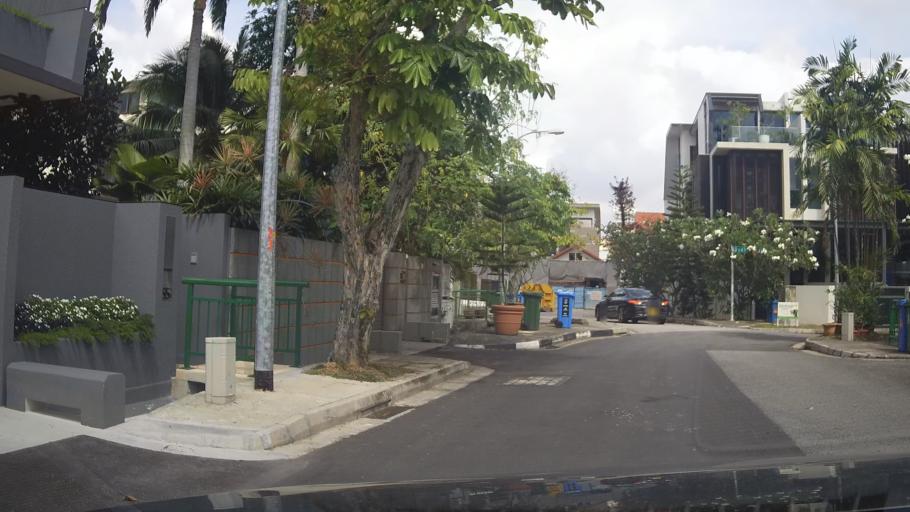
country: SG
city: Singapore
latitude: 1.3147
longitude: 103.9158
